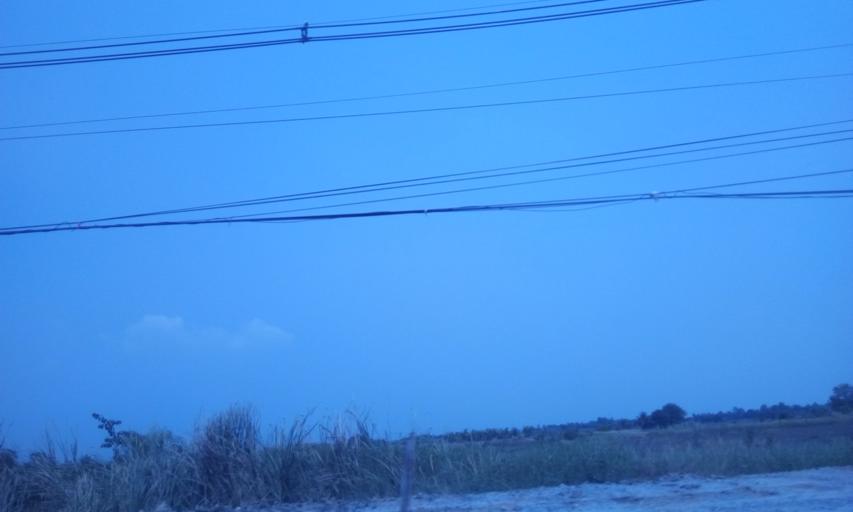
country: TH
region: Chachoengsao
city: Ban Pho
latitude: 13.5439
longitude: 101.1449
